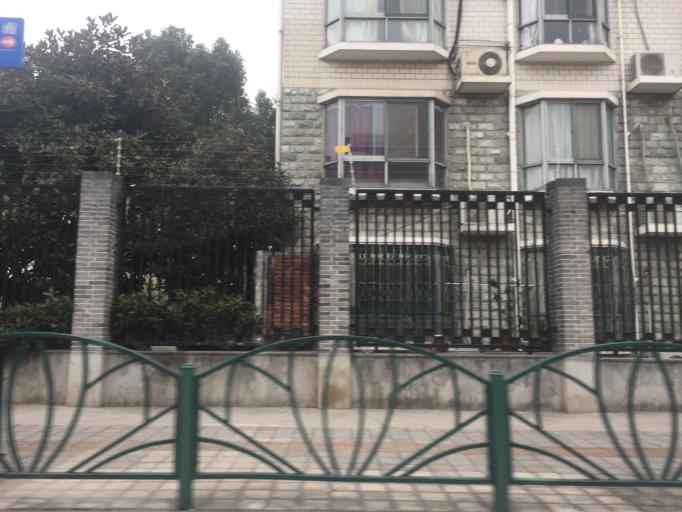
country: CN
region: Shanghai Shi
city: Luwan
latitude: 31.1856
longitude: 121.4940
